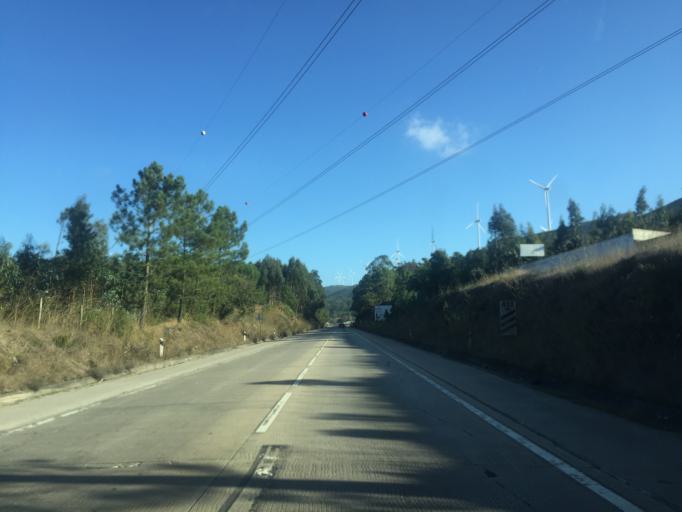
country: PT
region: Santarem
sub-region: Rio Maior
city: Rio Maior
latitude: 39.3703
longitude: -8.9670
